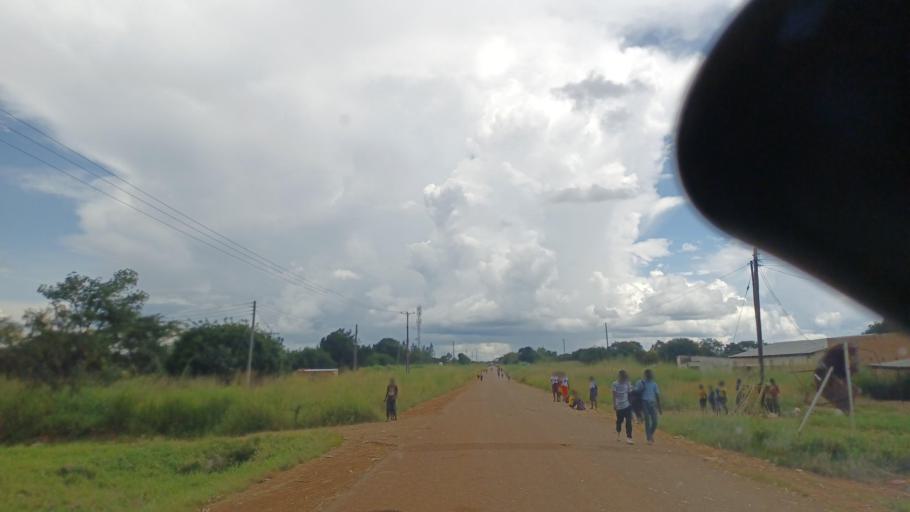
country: ZM
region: North-Western
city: Kasempa
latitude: -13.1046
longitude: 25.8707
